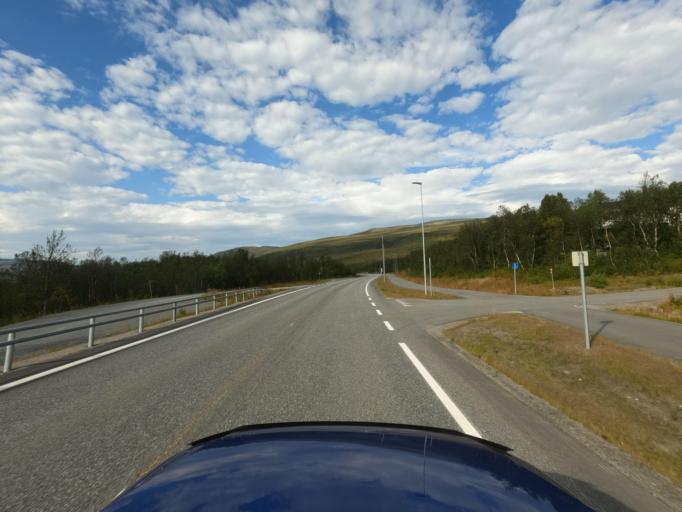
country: NO
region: Finnmark Fylke
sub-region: Kvalsund
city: Kvalsund
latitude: 70.4386
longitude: 24.4783
